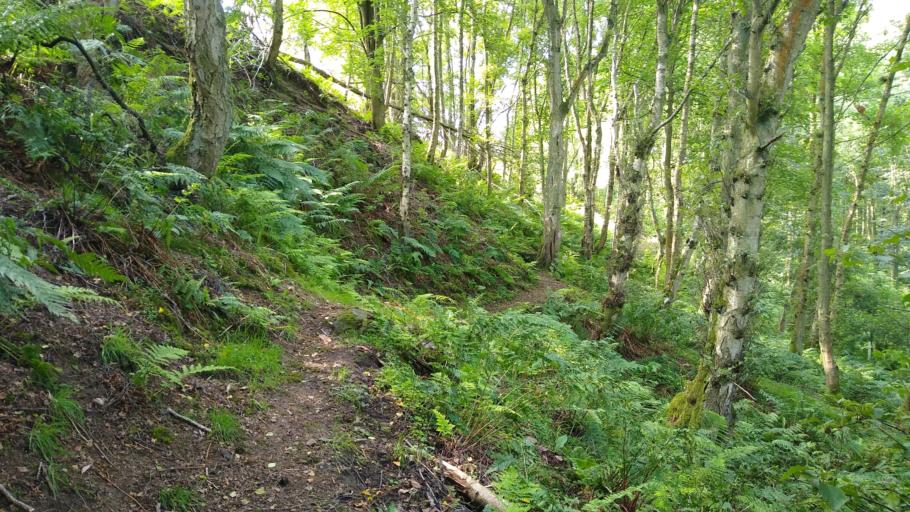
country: GB
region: England
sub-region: Northumberland
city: Haltwhistle
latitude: 54.9599
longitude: -2.4665
